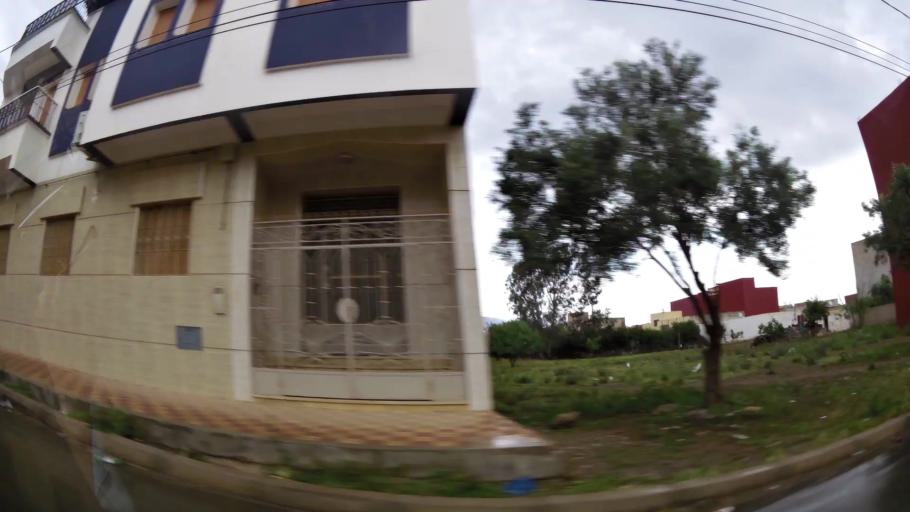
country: MA
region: Oriental
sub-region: Nador
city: Nador
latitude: 35.1498
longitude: -2.9914
